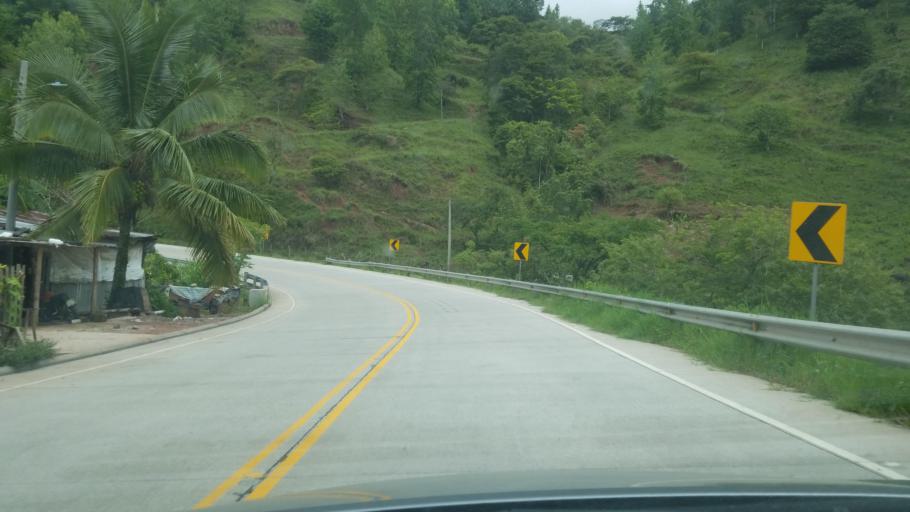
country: HN
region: Copan
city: San Jeronimo
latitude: 14.9339
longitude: -88.9545
